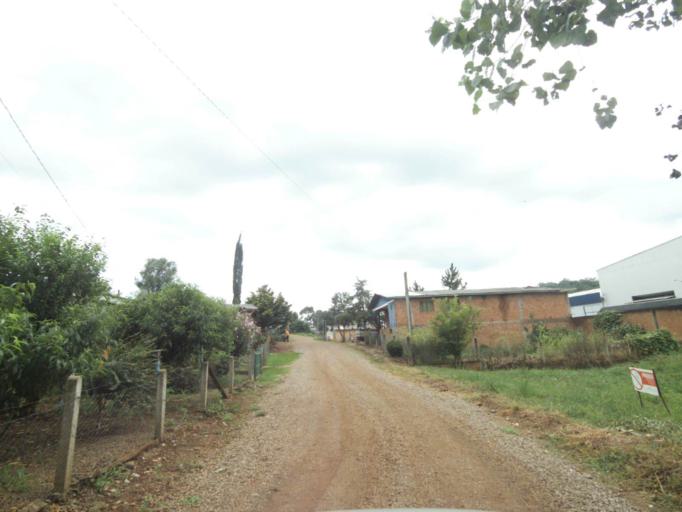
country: BR
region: Rio Grande do Sul
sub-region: Lagoa Vermelha
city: Lagoa Vermelha
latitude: -28.2307
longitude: -51.5168
